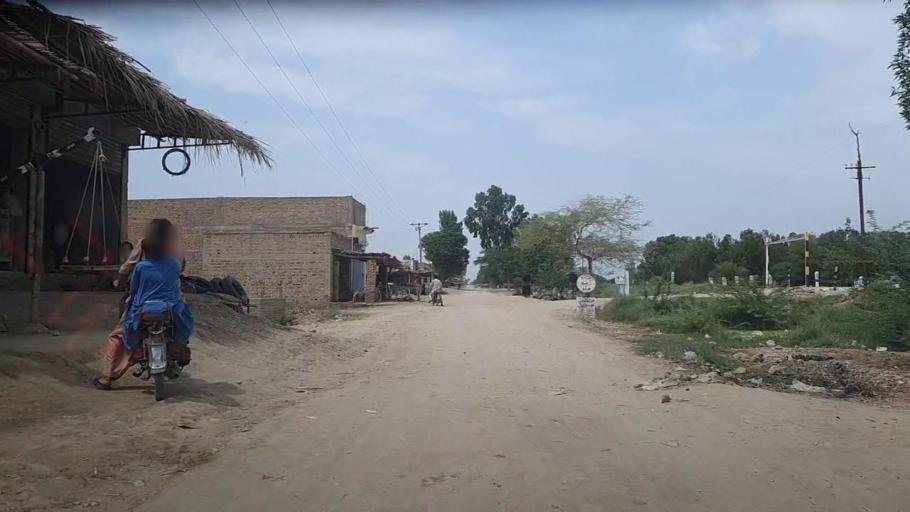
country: PK
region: Sindh
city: Bhiria
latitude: 26.8955
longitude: 68.2864
